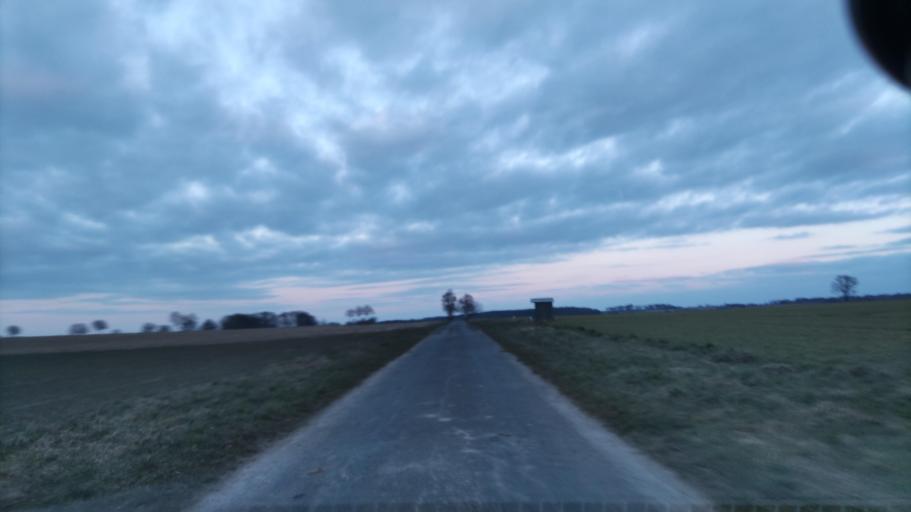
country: DE
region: Lower Saxony
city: Natendorf
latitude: 53.0656
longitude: 10.4379
